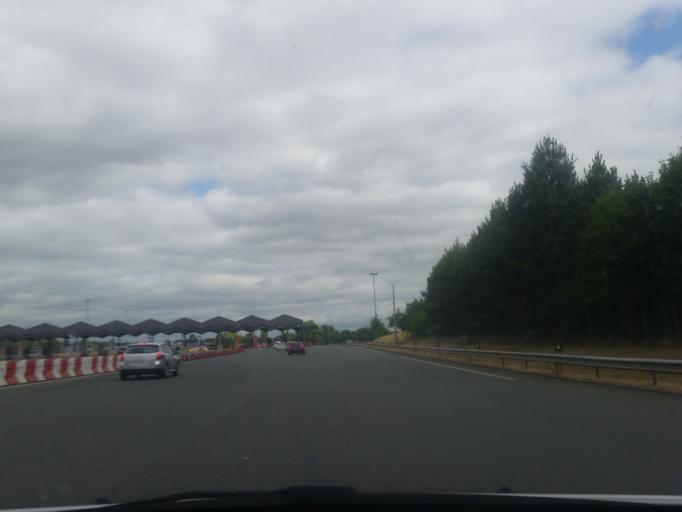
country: FR
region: Pays de la Loire
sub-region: Departement de Maine-et-Loire
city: Seiches-sur-le-Loir
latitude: 47.5373
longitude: -0.3417
